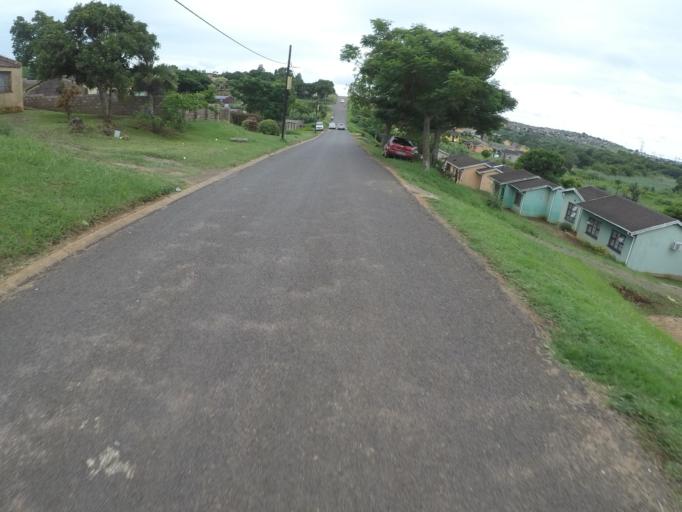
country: ZA
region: KwaZulu-Natal
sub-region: uThungulu District Municipality
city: Empangeni
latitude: -28.7721
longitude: 31.8666
